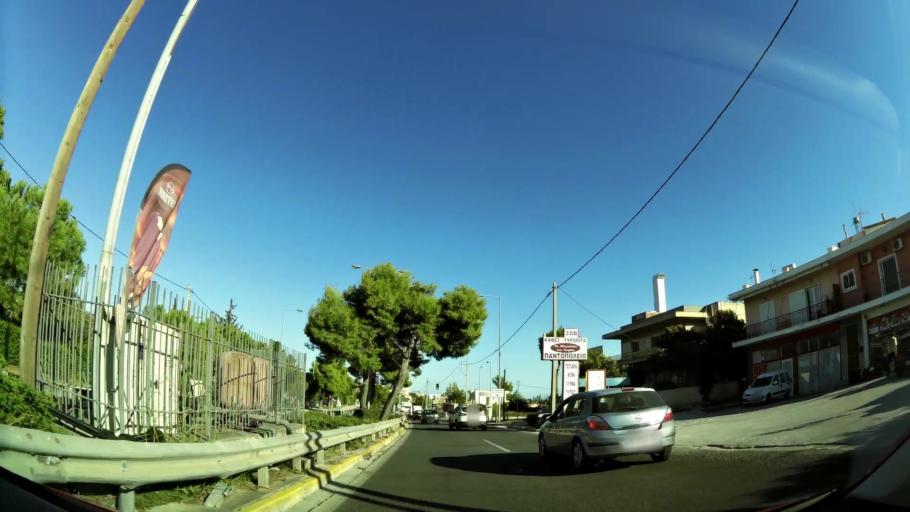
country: GR
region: Attica
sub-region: Nomarchia Anatolikis Attikis
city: Dhrafi
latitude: 38.0025
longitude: 23.9050
